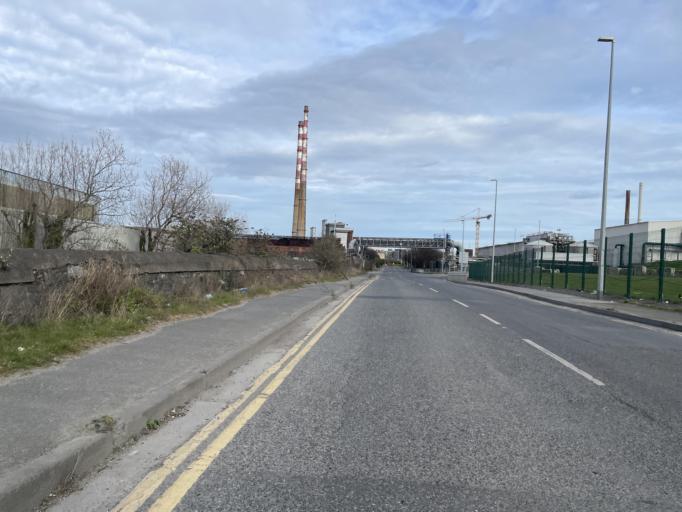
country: IE
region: Leinster
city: Sandymount
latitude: 53.3407
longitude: -6.2005
